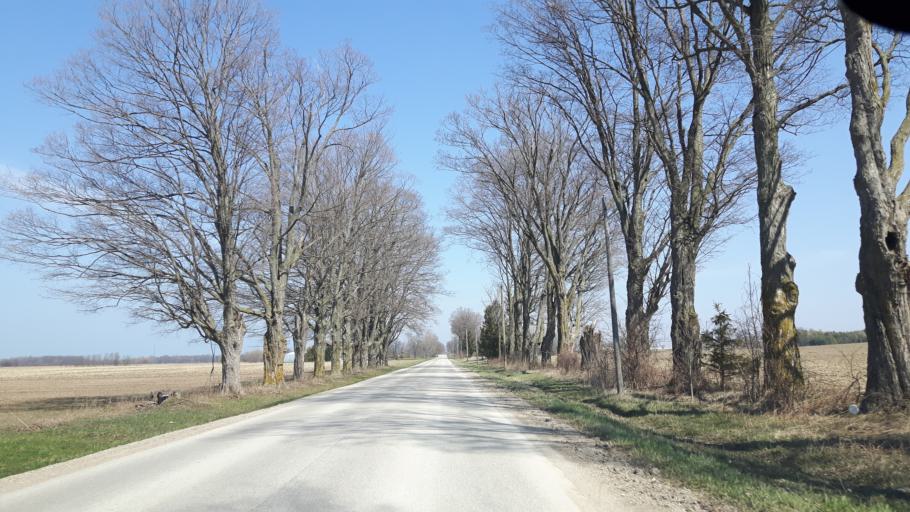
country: CA
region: Ontario
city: Goderich
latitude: 43.6936
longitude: -81.6848
